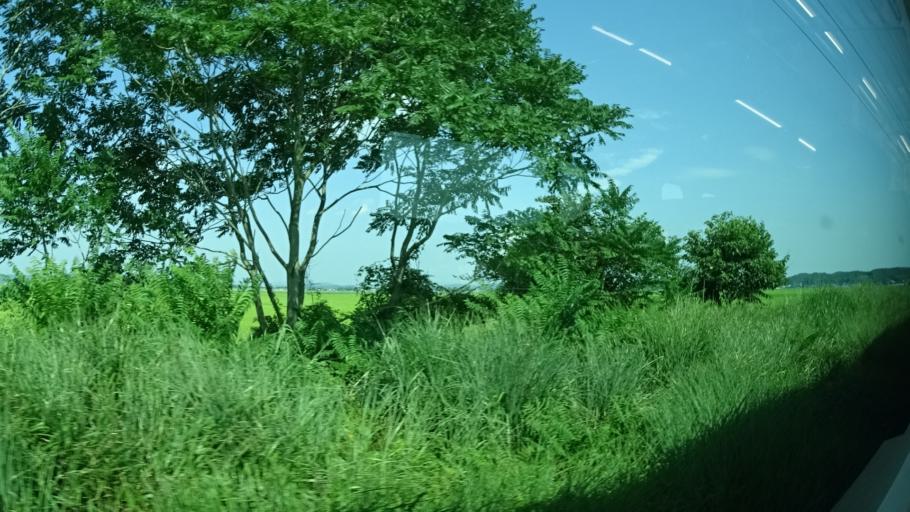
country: JP
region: Miyagi
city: Kogota
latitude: 38.5115
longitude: 141.0761
